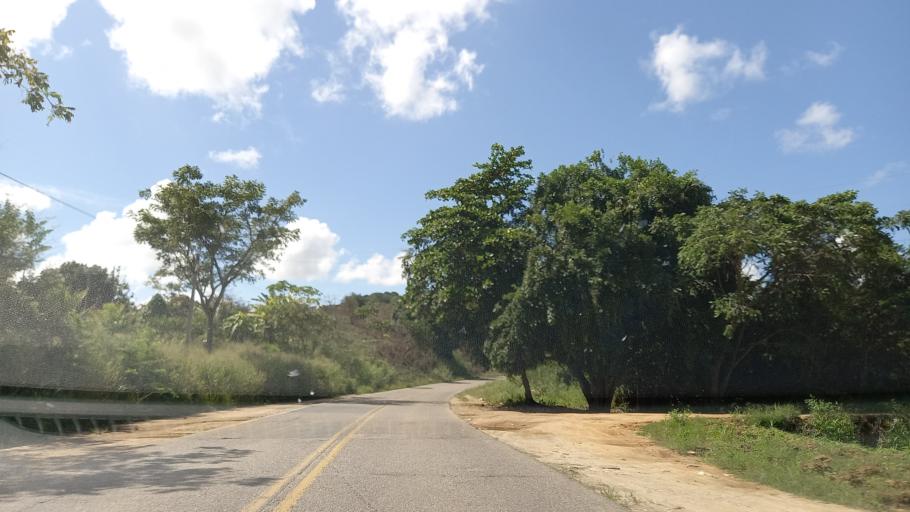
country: BR
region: Pernambuco
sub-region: Barreiros
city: Barreiros
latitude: -8.7742
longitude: -35.1733
